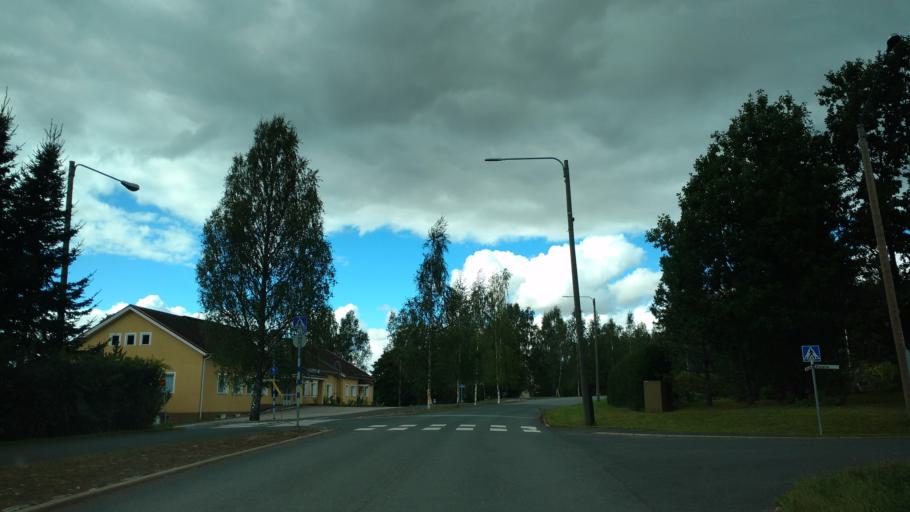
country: FI
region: Haeme
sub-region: Forssa
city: Ypaejae
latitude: 60.8049
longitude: 23.2753
